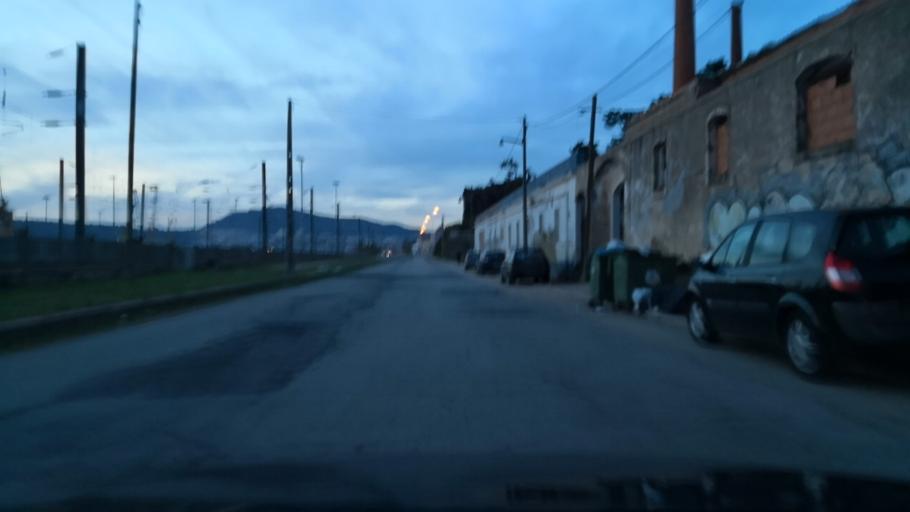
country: PT
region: Setubal
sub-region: Setubal
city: Setubal
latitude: 38.5183
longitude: -8.8740
